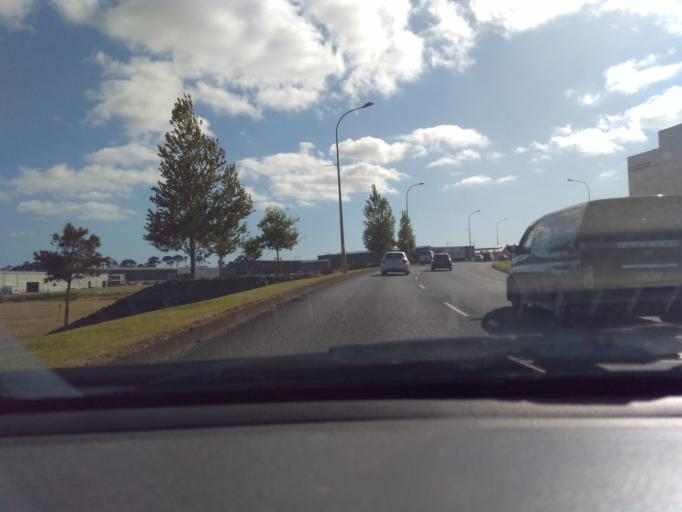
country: NZ
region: Auckland
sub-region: Auckland
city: Tamaki
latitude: -36.9367
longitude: 174.8737
